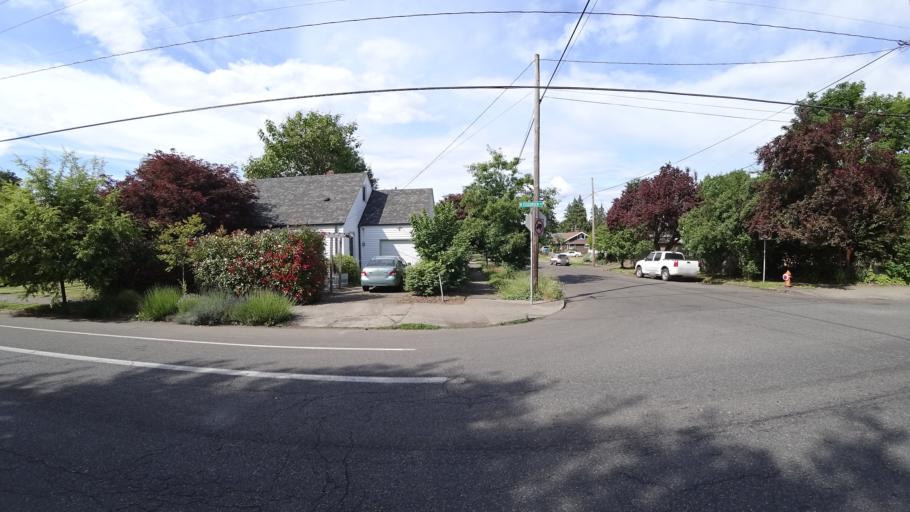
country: US
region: Oregon
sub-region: Washington County
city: West Haven
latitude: 45.5947
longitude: -122.7404
